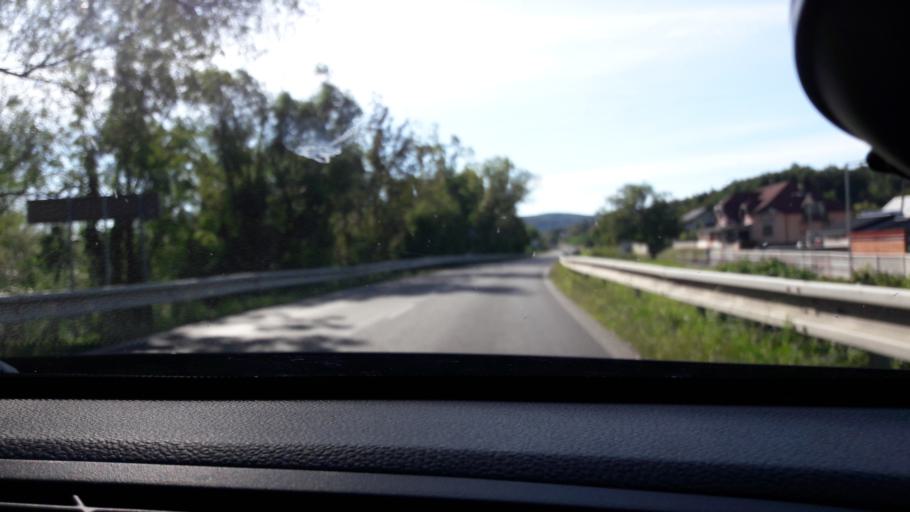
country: SK
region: Kosicky
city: Vinne
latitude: 48.8099
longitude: 22.0270
